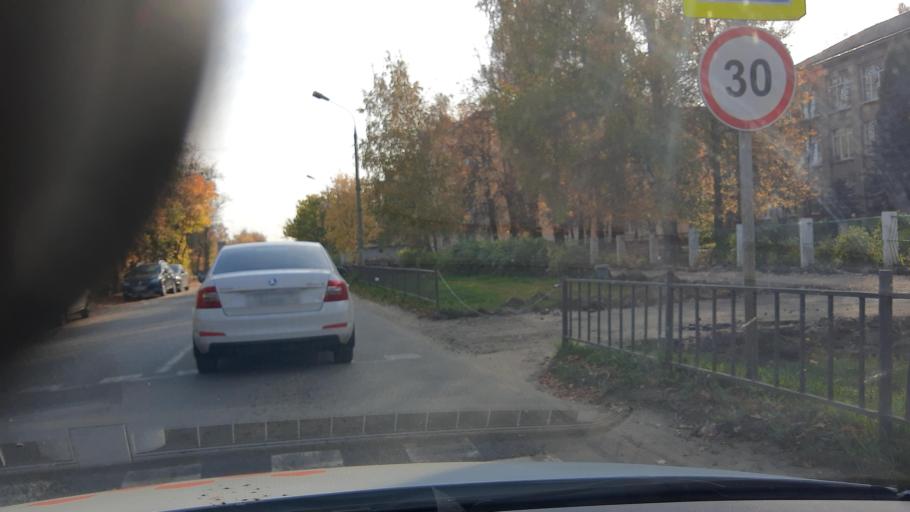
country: RU
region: Moskovskaya
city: Elektrostal'
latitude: 55.8006
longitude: 38.4424
